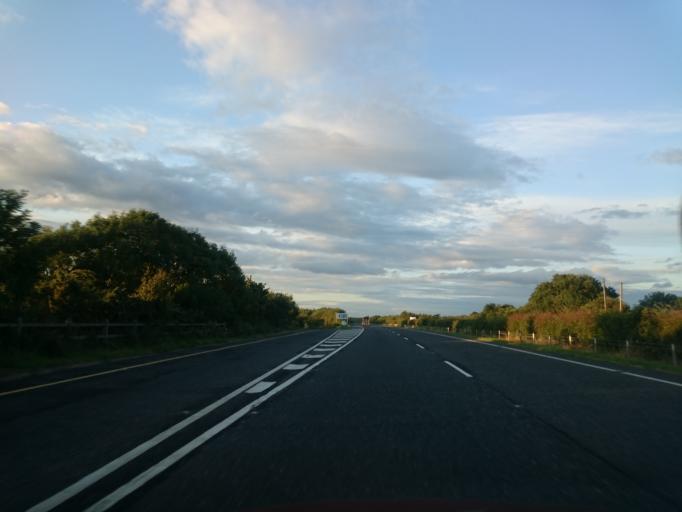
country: IE
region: Leinster
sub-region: Loch Garman
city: Castletown
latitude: 52.7707
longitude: -6.1862
